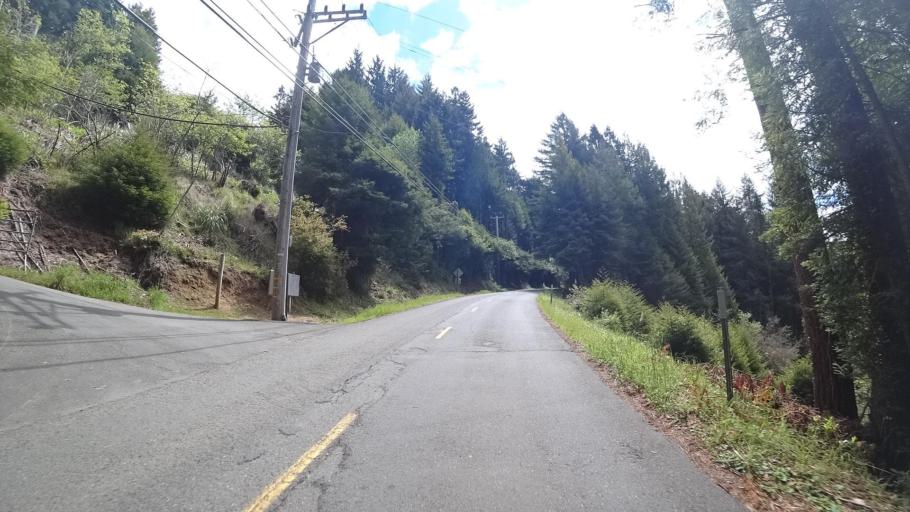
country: US
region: California
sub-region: Humboldt County
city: Arcata
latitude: 40.8691
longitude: -124.0579
